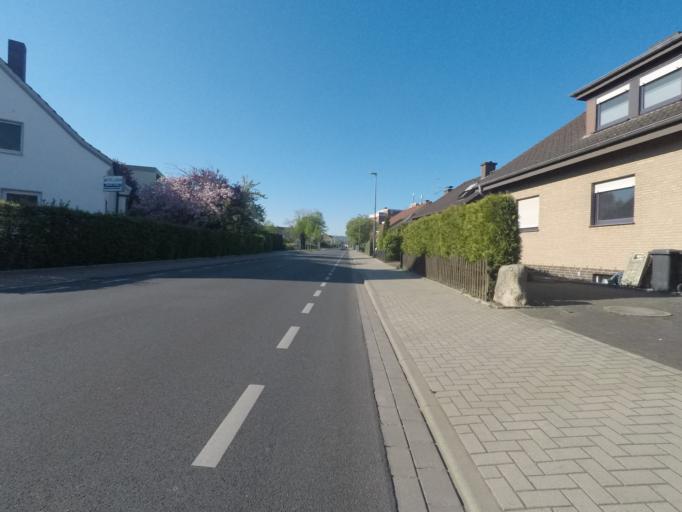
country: DE
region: North Rhine-Westphalia
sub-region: Regierungsbezirk Detmold
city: Bielefeld
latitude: 52.0214
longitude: 8.5999
